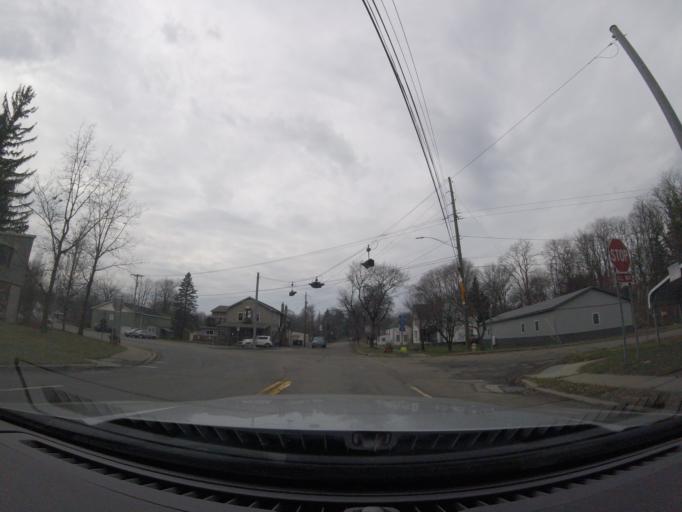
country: US
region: New York
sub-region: Schuyler County
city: Watkins Glen
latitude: 42.4203
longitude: -76.8485
